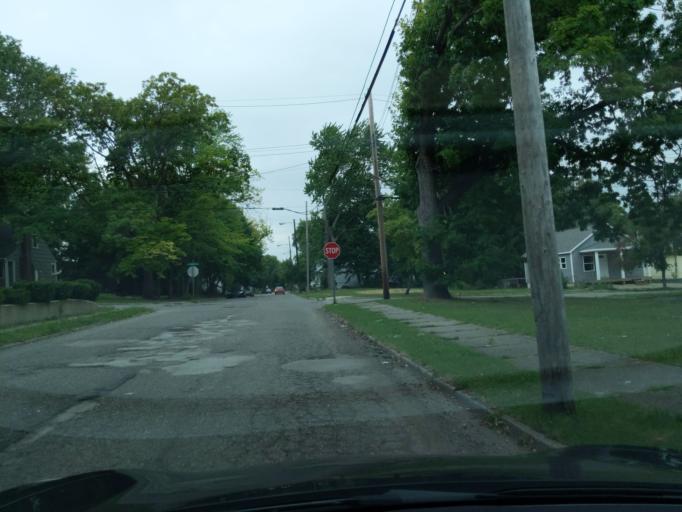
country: US
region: Michigan
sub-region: Ingham County
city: Lansing
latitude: 42.7226
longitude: -84.5304
